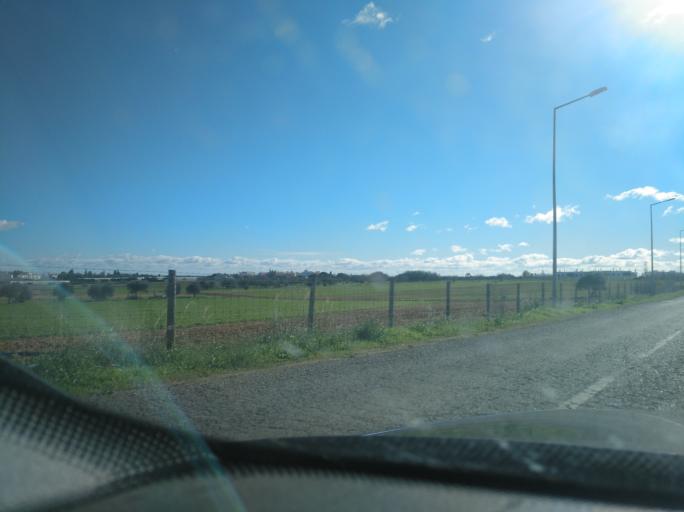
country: PT
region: Faro
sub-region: Vila Real de Santo Antonio
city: Monte Gordo
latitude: 37.1750
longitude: -7.5200
